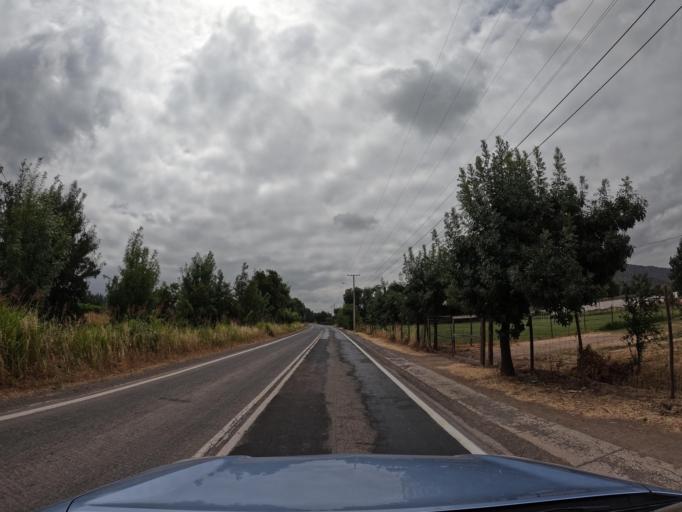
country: CL
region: Maule
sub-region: Provincia de Curico
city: Teno
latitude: -34.7502
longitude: -71.2305
